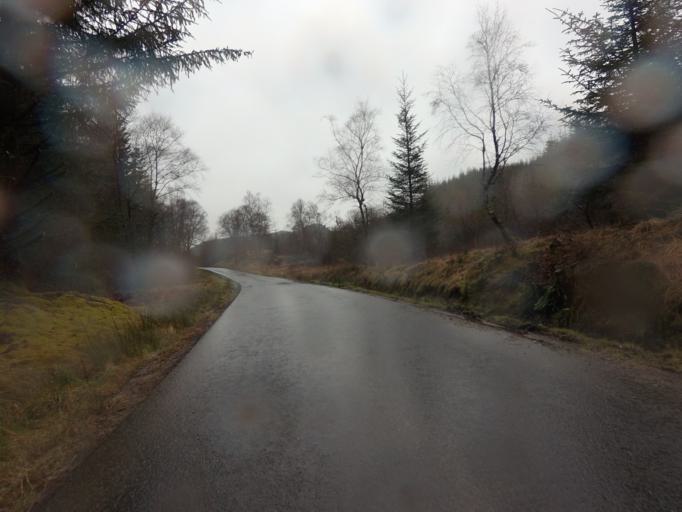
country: GB
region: Scotland
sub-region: West Dunbartonshire
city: Balloch
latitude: 56.2330
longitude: -4.5595
